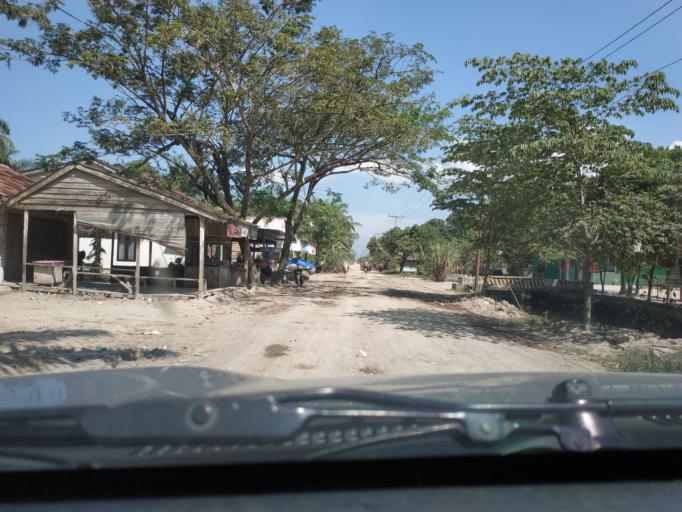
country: ID
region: North Sumatra
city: Tanjungbalai
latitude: 2.8723
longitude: 99.8605
